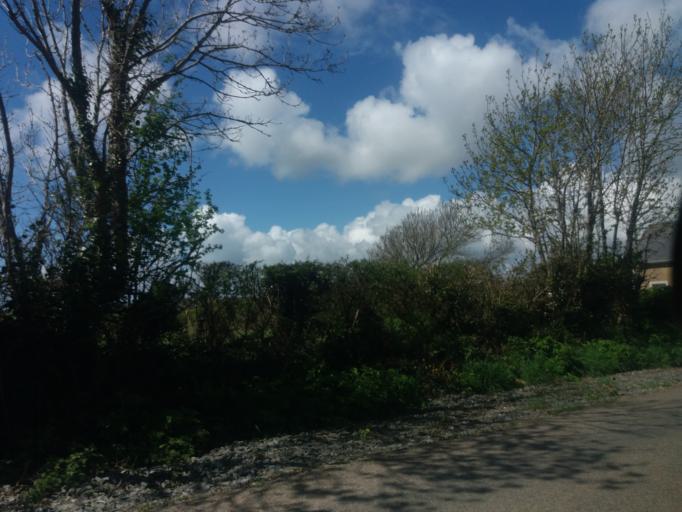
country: IE
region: Munster
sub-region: Waterford
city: Dunmore East
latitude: 52.2406
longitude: -6.8568
